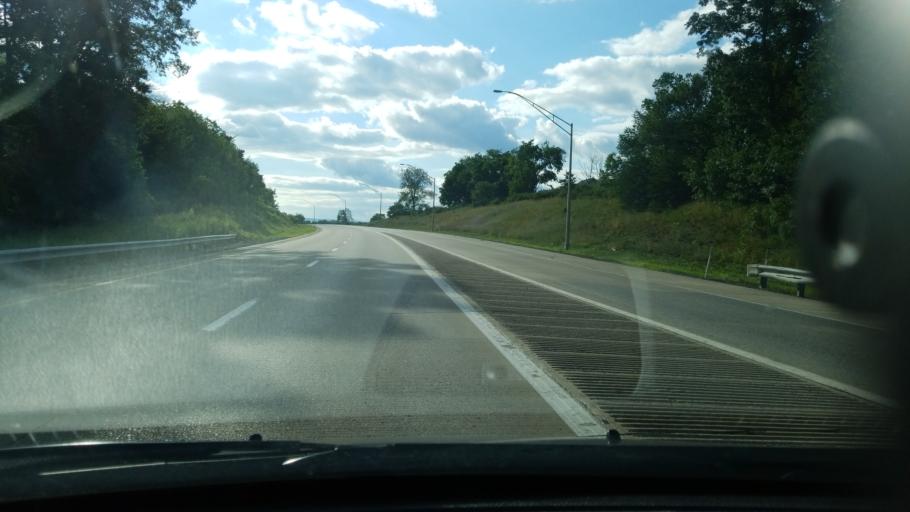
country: US
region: Pennsylvania
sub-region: Northumberland County
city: Riverside
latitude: 40.9910
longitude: -76.7288
